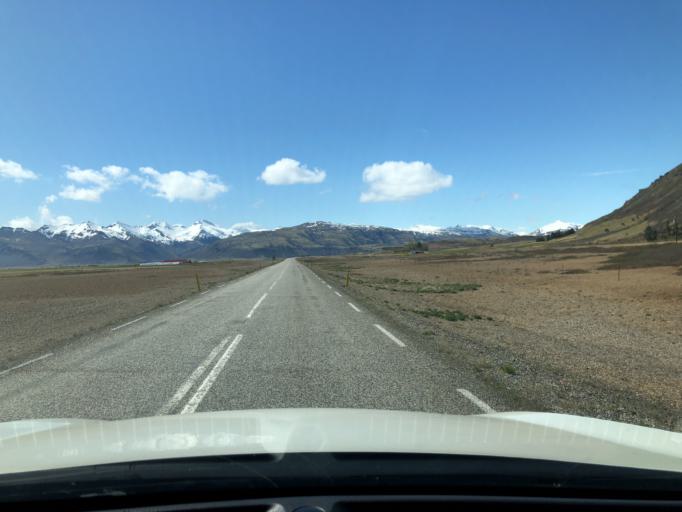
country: IS
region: East
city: Hoefn
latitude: 64.4262
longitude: -14.7941
